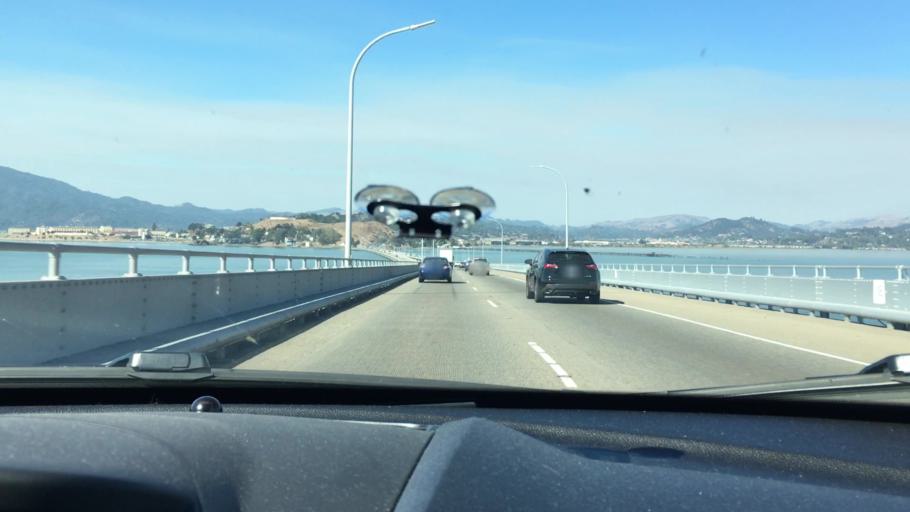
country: US
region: California
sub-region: Marin County
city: Strawberry
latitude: 37.9388
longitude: -122.4621
